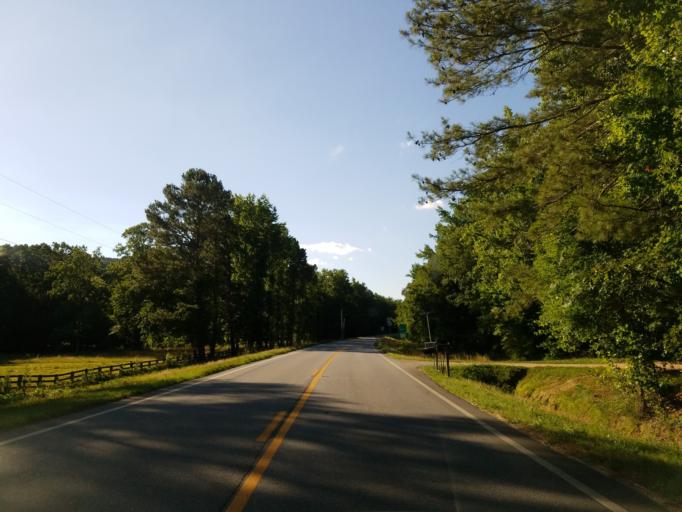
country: US
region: Georgia
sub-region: Gordon County
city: Calhoun
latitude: 34.6228
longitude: -85.0554
